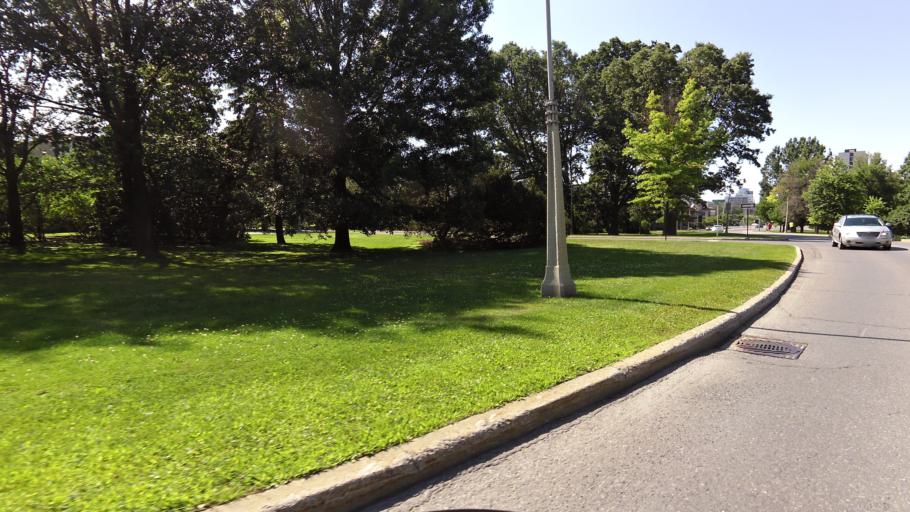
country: CA
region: Ontario
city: Ottawa
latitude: 45.4091
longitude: -75.6823
